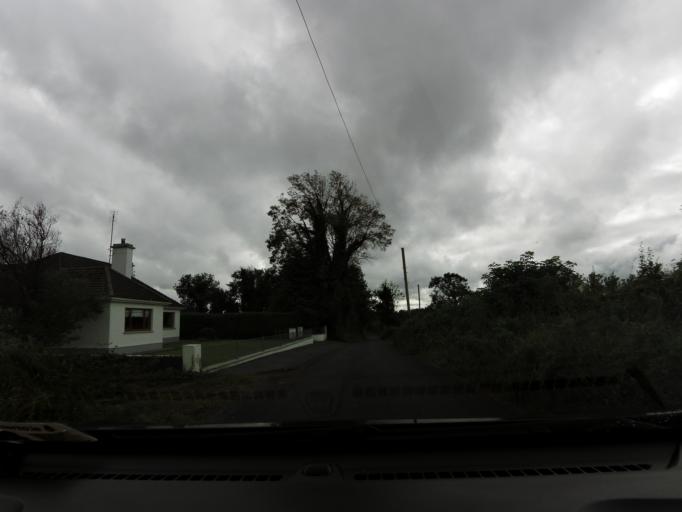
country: IE
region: Connaught
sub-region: County Galway
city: Loughrea
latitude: 53.2927
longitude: -8.5905
